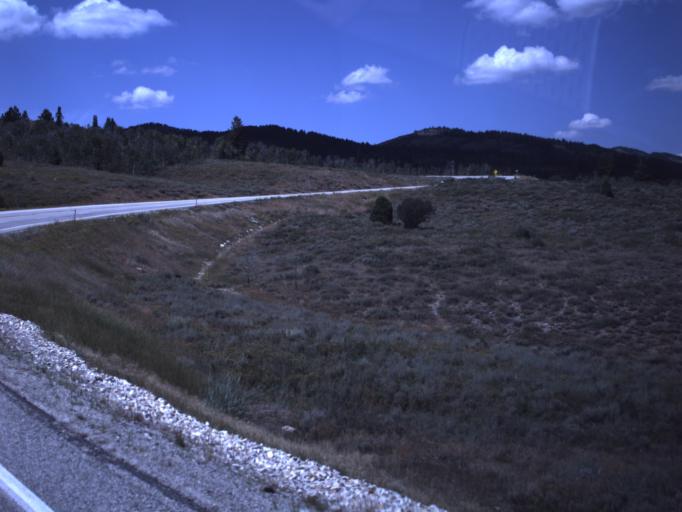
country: US
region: Idaho
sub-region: Bear Lake County
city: Paris
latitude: 41.9291
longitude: -111.4431
